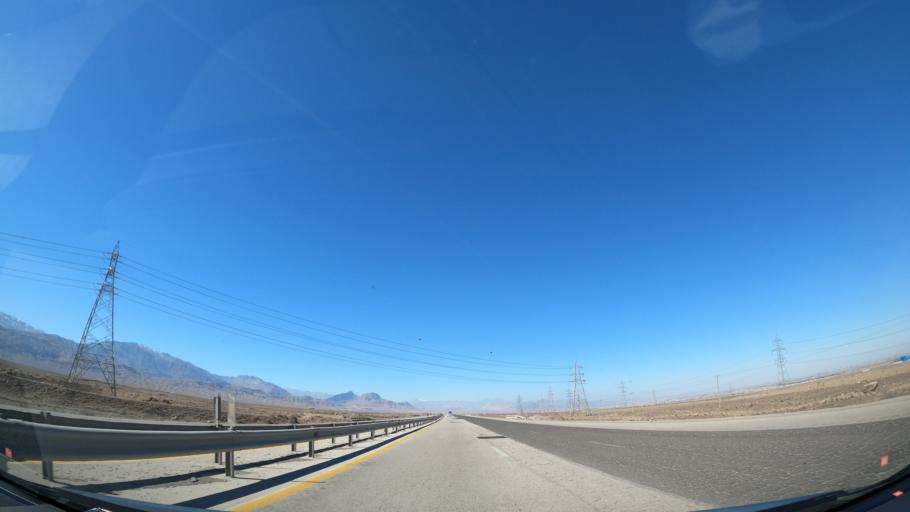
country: IR
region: Isfahan
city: Kashan
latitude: 33.8734
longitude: 51.5066
